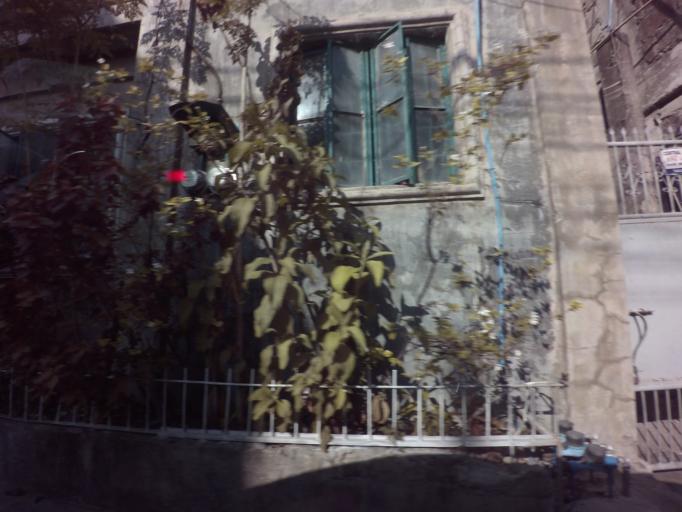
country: PH
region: Calabarzon
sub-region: Province of Rizal
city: Taguig
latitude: 14.4956
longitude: 121.0524
